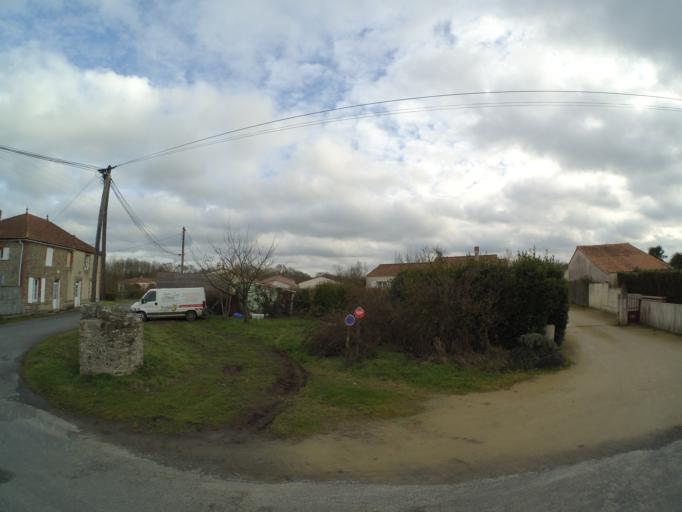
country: FR
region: Pays de la Loire
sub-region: Departement de la Vendee
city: La Bernardiere
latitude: 47.0475
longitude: -1.2869
